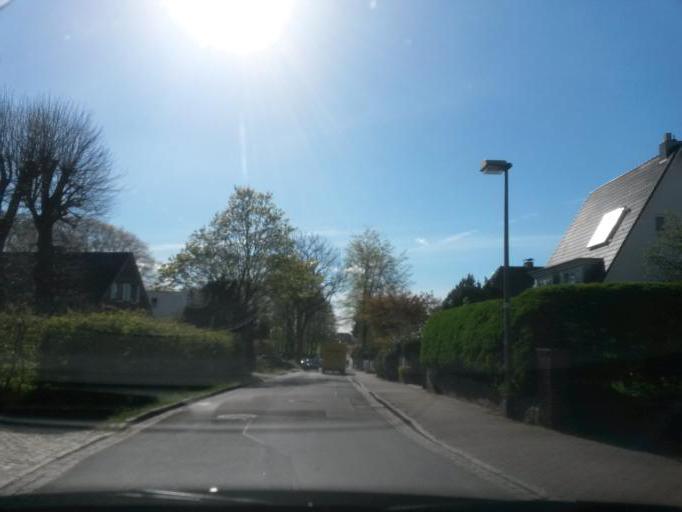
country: DE
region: Schleswig-Holstein
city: Wedel
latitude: 53.5736
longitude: 9.7022
